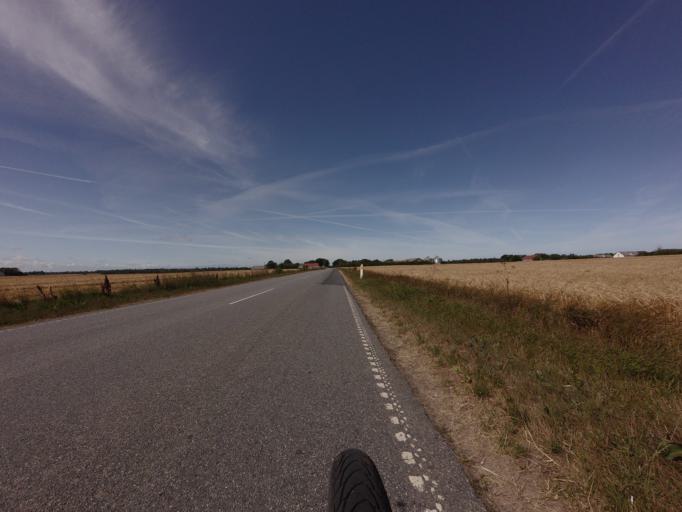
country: DK
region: North Denmark
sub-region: Hjorring Kommune
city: Vra
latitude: 57.3321
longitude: 9.8142
